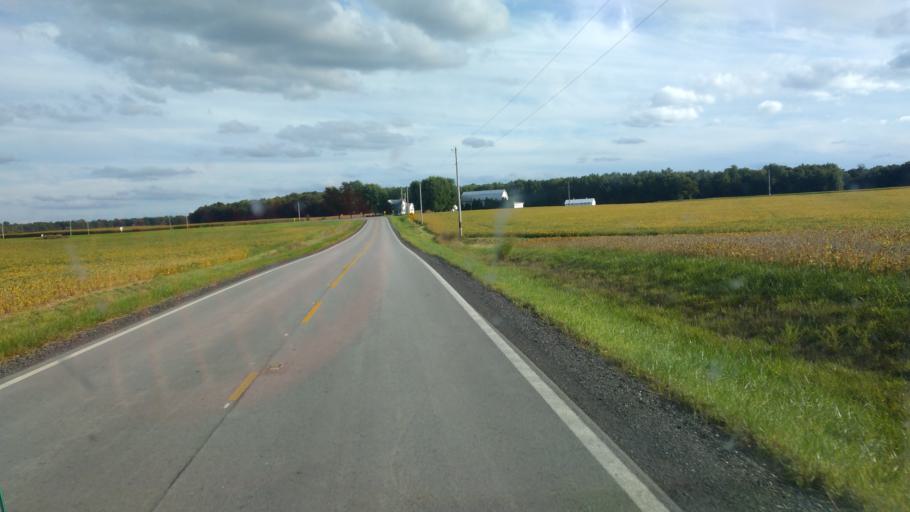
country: US
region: Ohio
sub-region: Crawford County
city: Bucyrus
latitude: 40.9239
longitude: -83.0482
